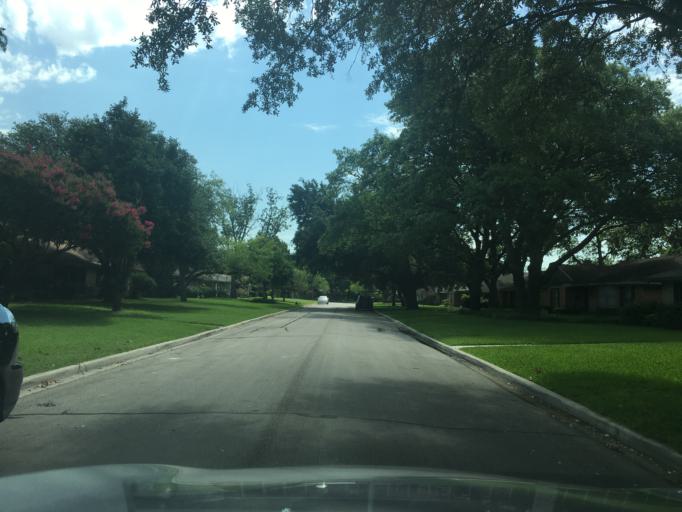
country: US
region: Texas
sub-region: Dallas County
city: Farmers Branch
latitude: 32.9296
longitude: -96.8662
